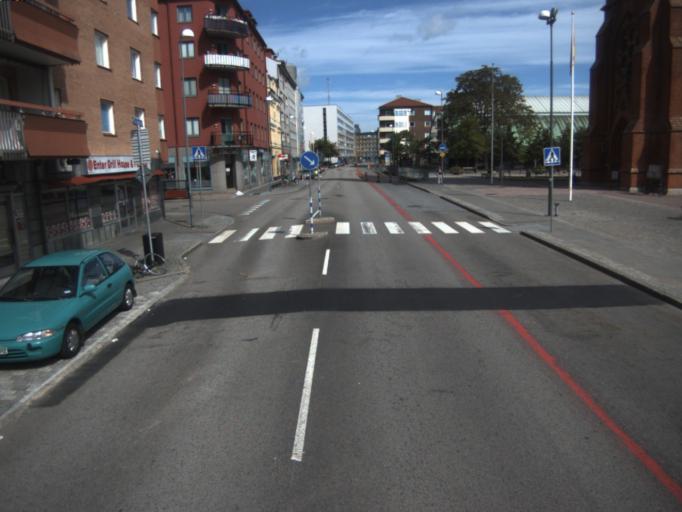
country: SE
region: Skane
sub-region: Helsingborg
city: Helsingborg
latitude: 56.0380
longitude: 12.7021
